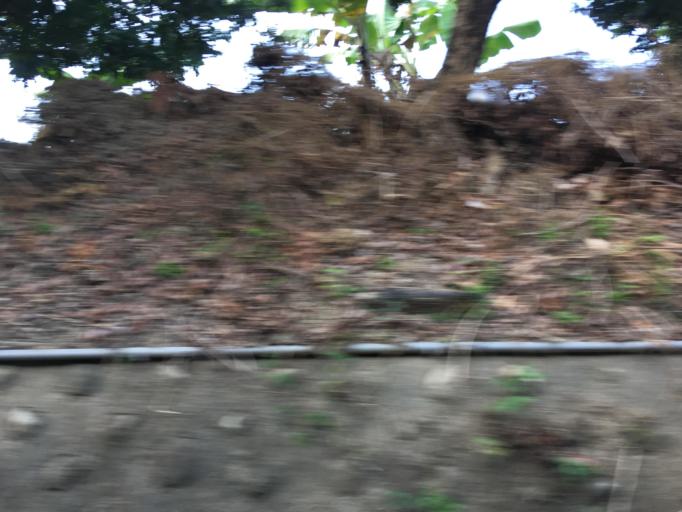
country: TW
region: Taiwan
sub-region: Chiayi
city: Jiayi Shi
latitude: 23.4959
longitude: 120.5233
